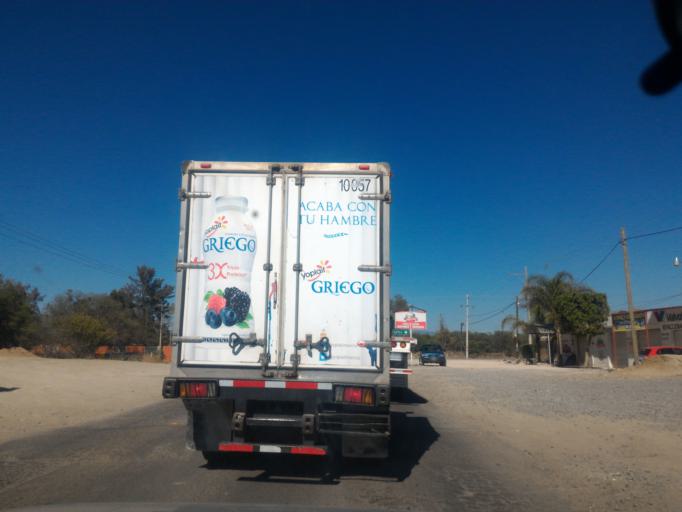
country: MX
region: Guanajuato
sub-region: Leon
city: Malagana (San Antonio del Monte)
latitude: 21.0324
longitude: -101.7768
